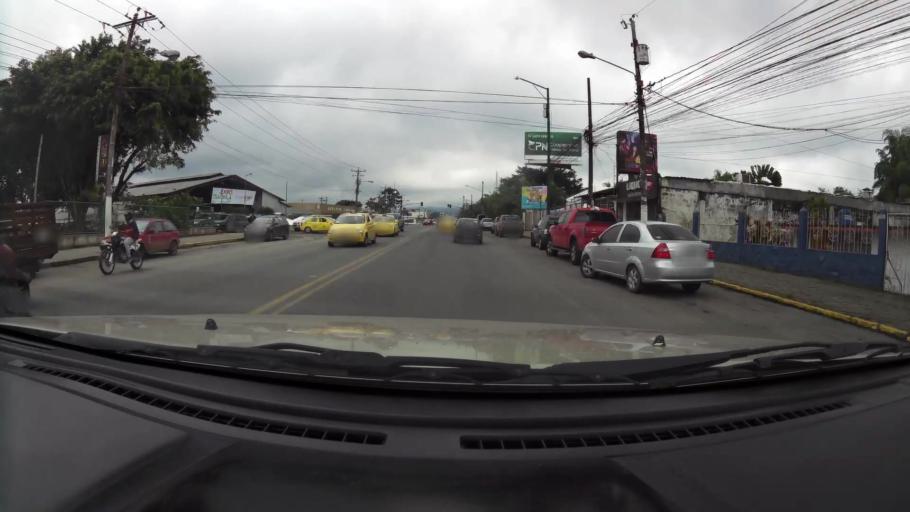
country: EC
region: Santo Domingo de los Tsachilas
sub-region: Canton Santo Domingo de los Colorados
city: Santo Domingo de los Colorados
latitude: -0.2482
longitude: -79.1564
